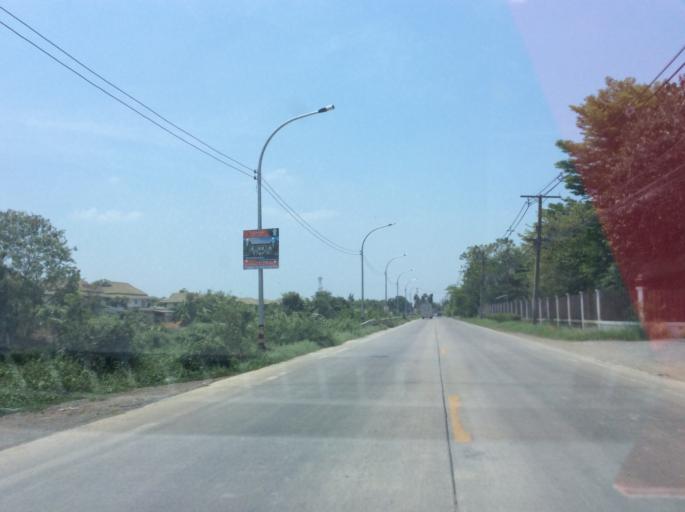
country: TH
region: Pathum Thani
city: Ban Rangsit
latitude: 14.0311
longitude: 100.7788
